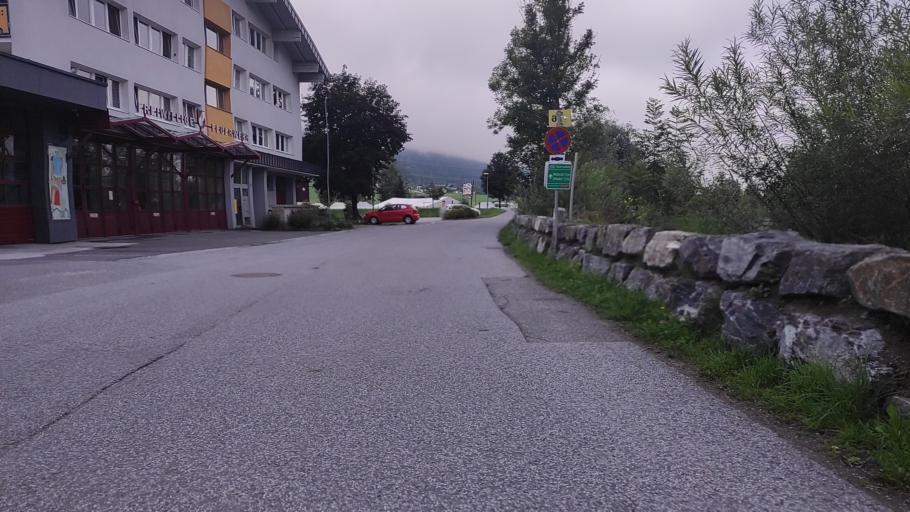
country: AT
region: Salzburg
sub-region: Politischer Bezirk Zell am See
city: Niedernsill
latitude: 47.2807
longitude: 12.6461
